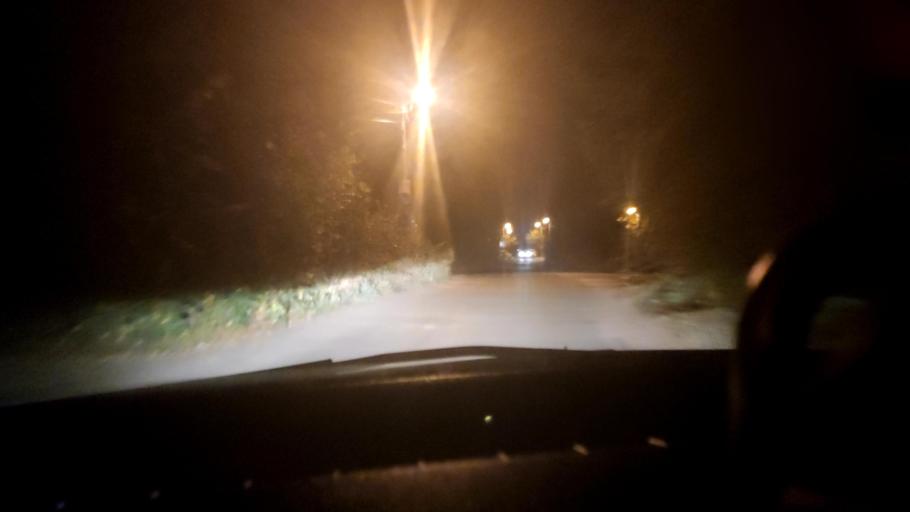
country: RU
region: Voronezj
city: Voronezh
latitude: 51.6320
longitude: 39.1837
